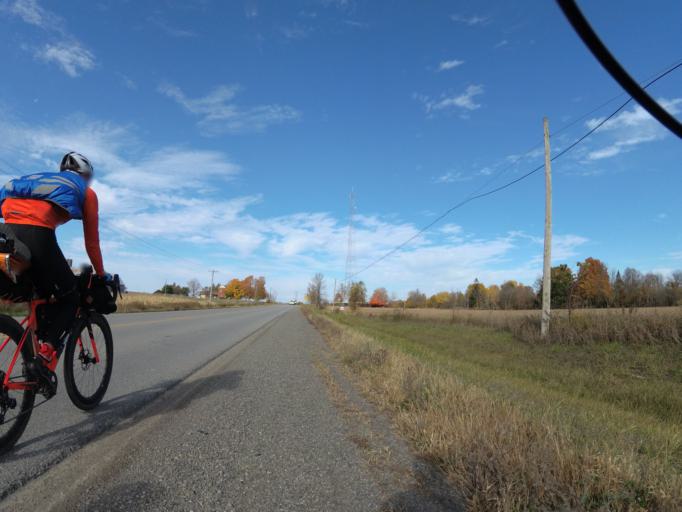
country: CA
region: Ontario
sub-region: Lanark County
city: Smiths Falls
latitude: 44.8895
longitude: -76.0090
